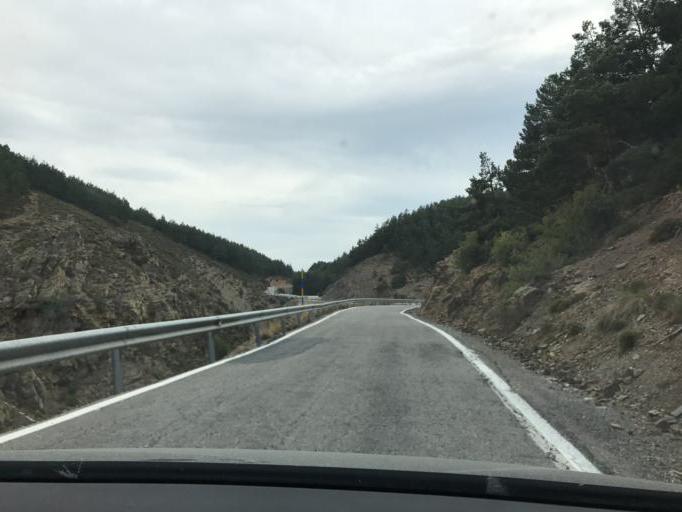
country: ES
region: Andalusia
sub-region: Provincia de Granada
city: Ferreira
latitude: 37.1219
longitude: -3.0343
